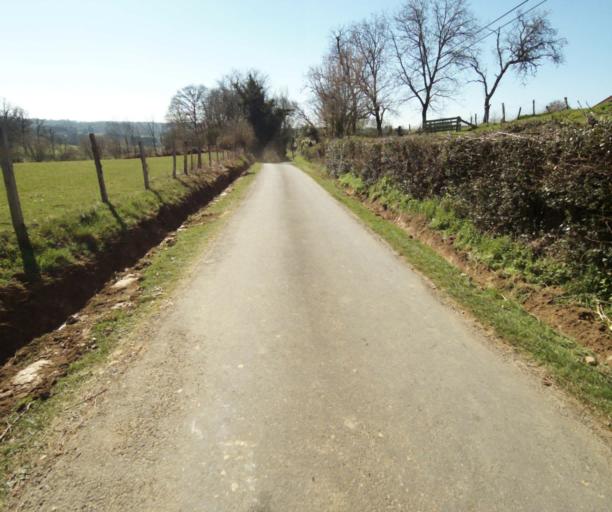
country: FR
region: Limousin
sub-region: Departement de la Correze
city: Saint-Clement
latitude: 45.3541
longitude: 1.6616
